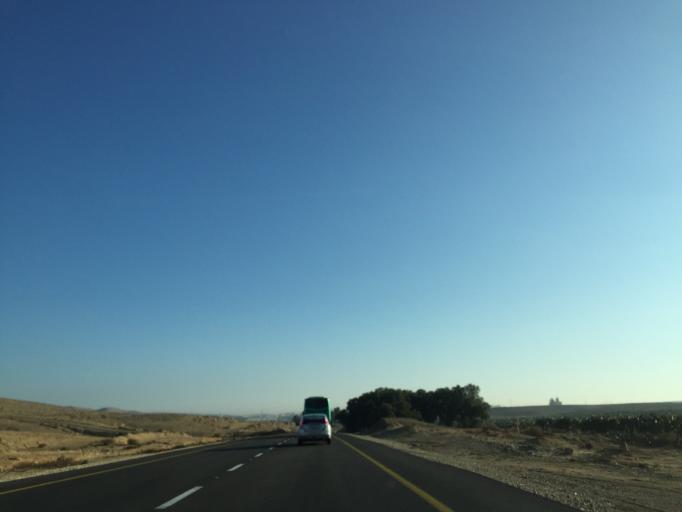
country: IL
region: Southern District
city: Dimona
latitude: 31.0499
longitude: 34.9906
